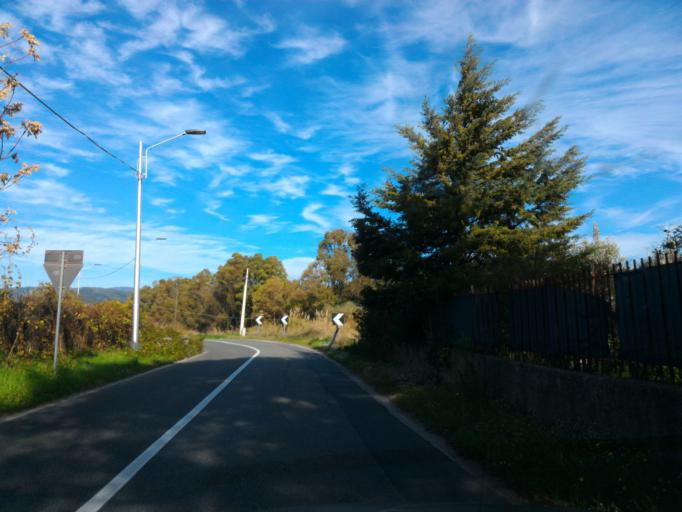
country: IT
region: Calabria
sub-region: Provincia di Catanzaro
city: Sellia Marina
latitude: 38.9063
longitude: 16.7618
